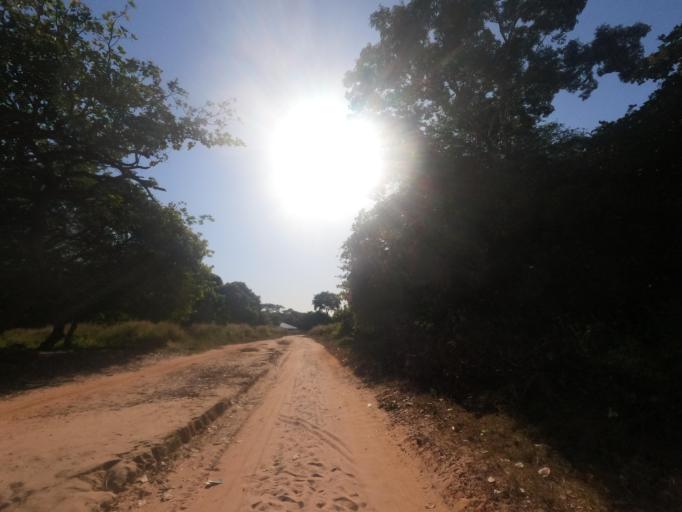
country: GW
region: Cacheu
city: Cacheu
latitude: 12.3932
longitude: -16.2190
